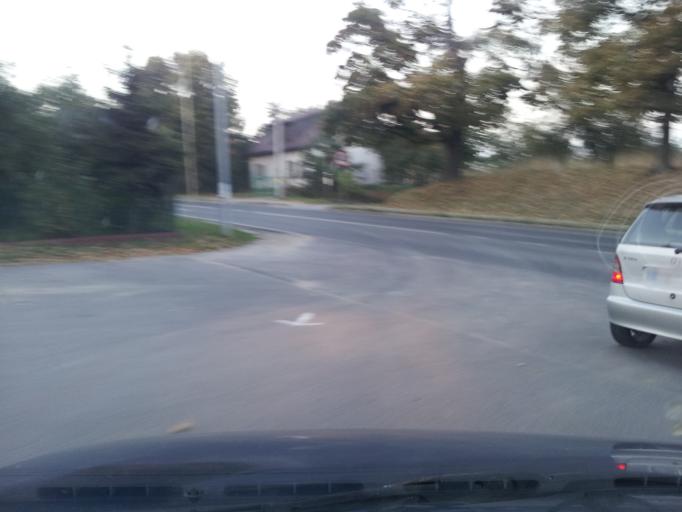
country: PL
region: Kujawsko-Pomorskie
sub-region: Powiat golubsko-dobrzynski
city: Golub-Dobrzyn
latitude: 53.1167
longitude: 19.0465
